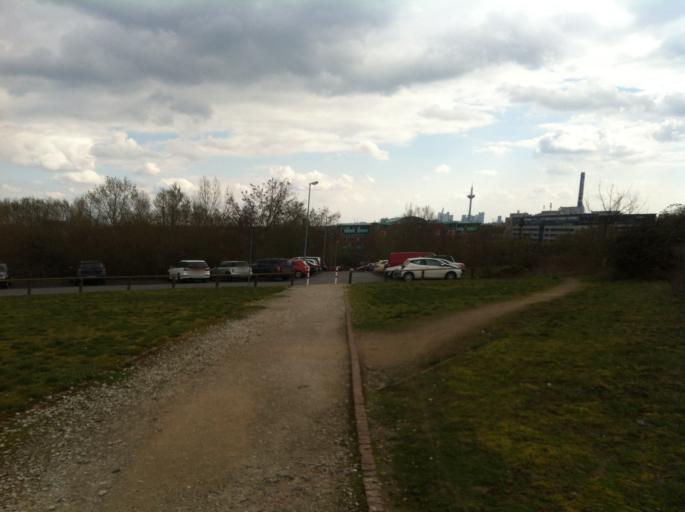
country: DE
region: Hesse
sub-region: Regierungsbezirk Darmstadt
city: Bad Homburg vor der Hoehe
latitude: 50.1718
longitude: 8.6322
